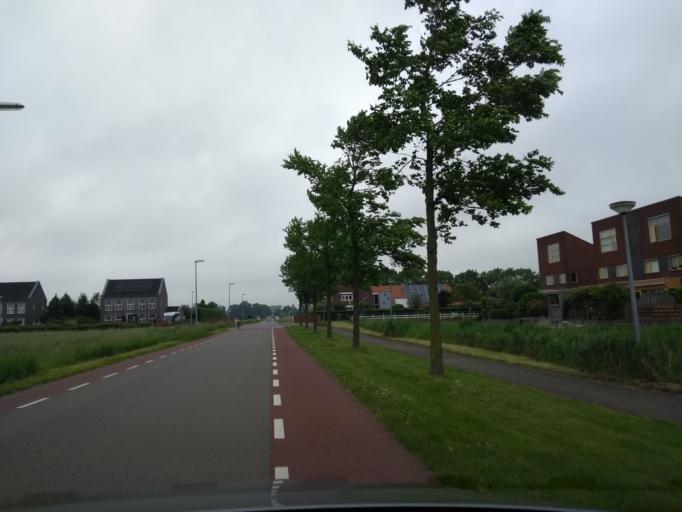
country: NL
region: Groningen
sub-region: Gemeente Groningen
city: Korrewegwijk
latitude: 53.2451
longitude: 6.5186
